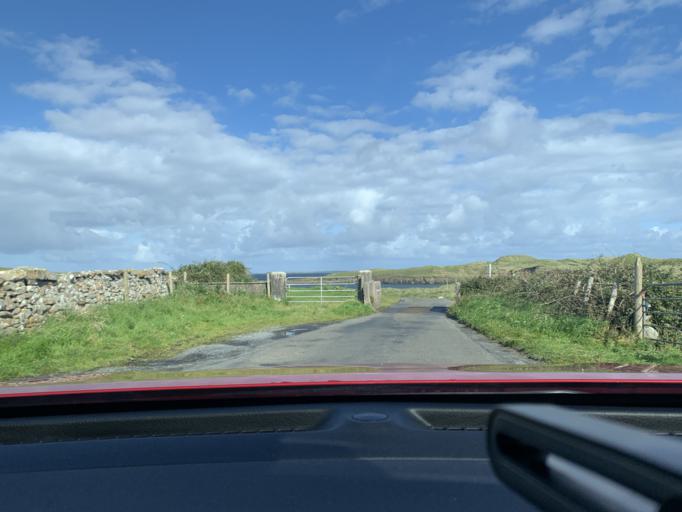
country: IE
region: Connaught
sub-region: Sligo
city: Strandhill
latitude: 54.3970
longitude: -8.5660
